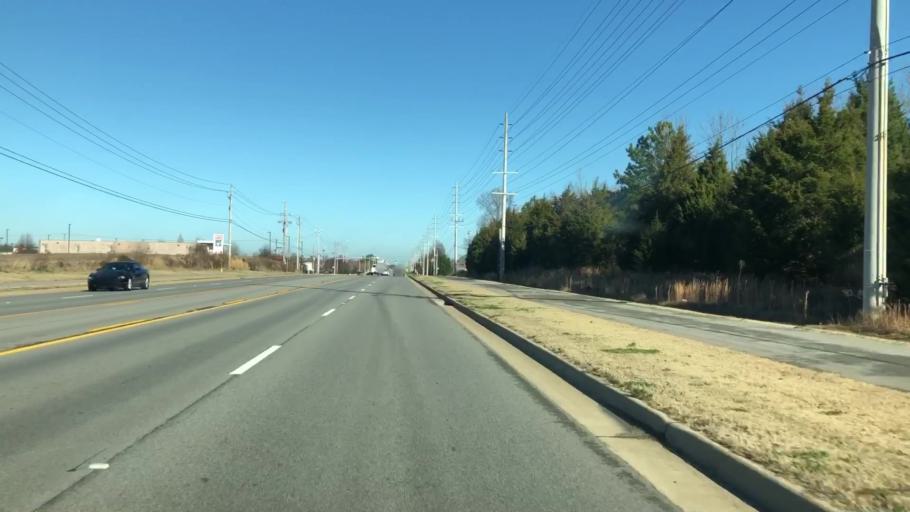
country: US
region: Alabama
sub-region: Madison County
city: Madison
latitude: 34.7264
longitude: -86.7863
